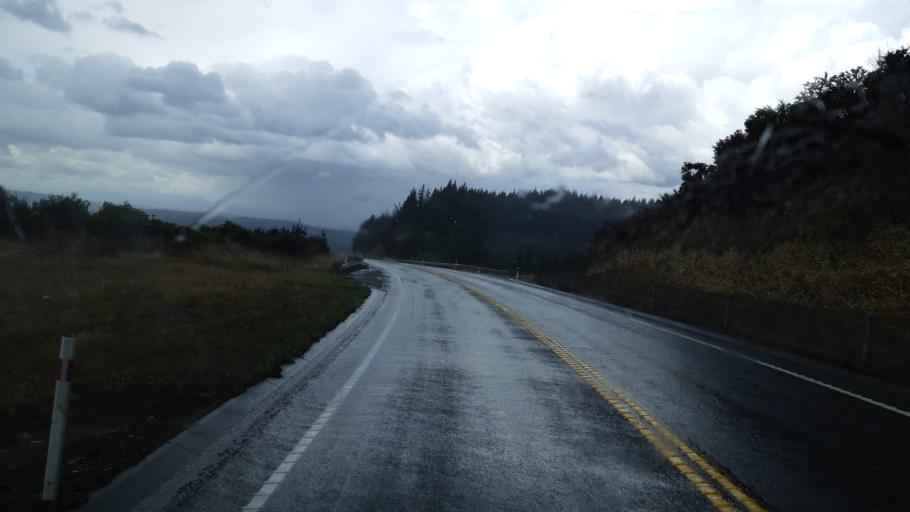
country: NZ
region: Tasman
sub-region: Tasman District
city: Wakefield
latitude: -41.4807
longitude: 172.9140
